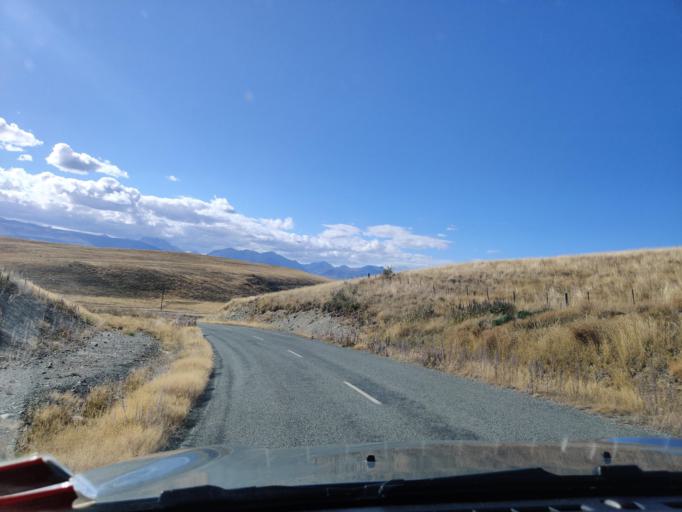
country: NZ
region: Canterbury
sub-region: Timaru District
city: Pleasant Point
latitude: -43.9757
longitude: 170.4642
